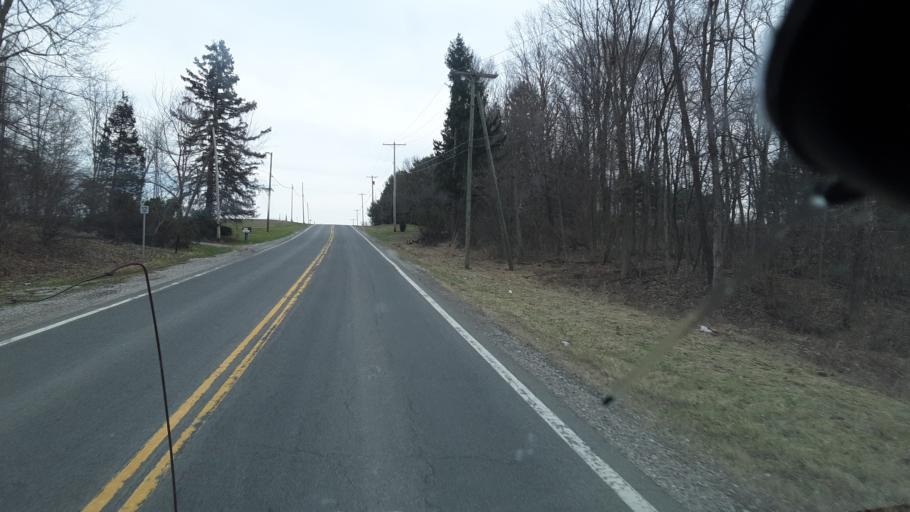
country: US
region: Ohio
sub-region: Huron County
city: Plymouth
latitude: 40.9654
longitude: -82.6674
